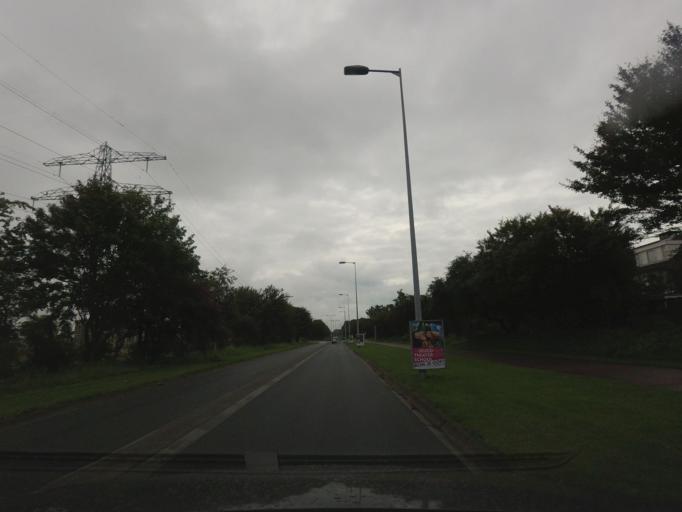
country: NL
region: North Holland
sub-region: Gemeente Heemstede
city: Heemstede
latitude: 52.3142
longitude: 4.6467
